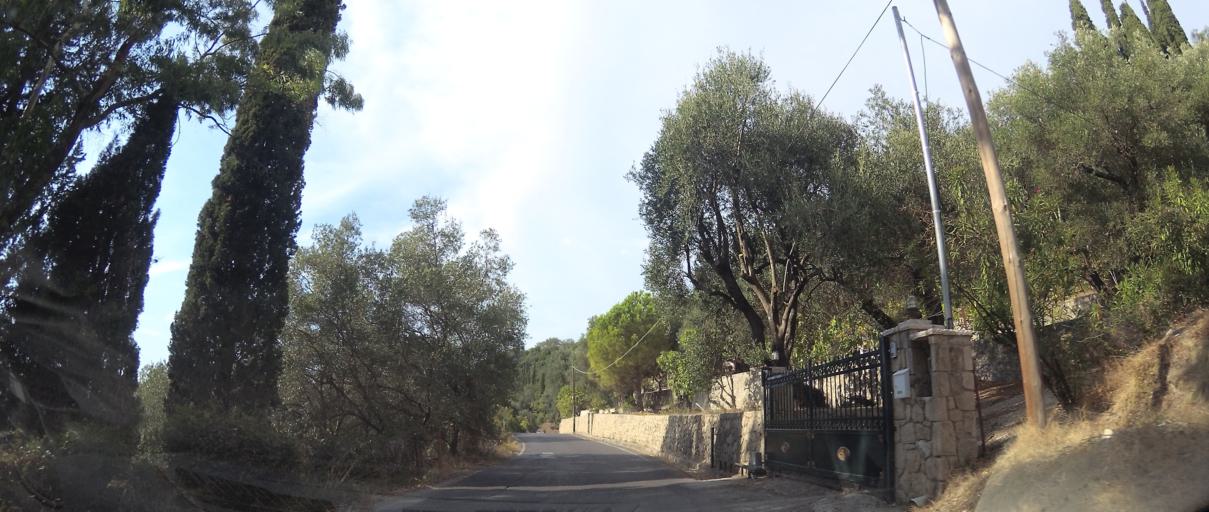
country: GR
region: Ionian Islands
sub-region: Nomos Kerkyras
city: Kynopiastes
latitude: 39.5486
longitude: 19.8664
